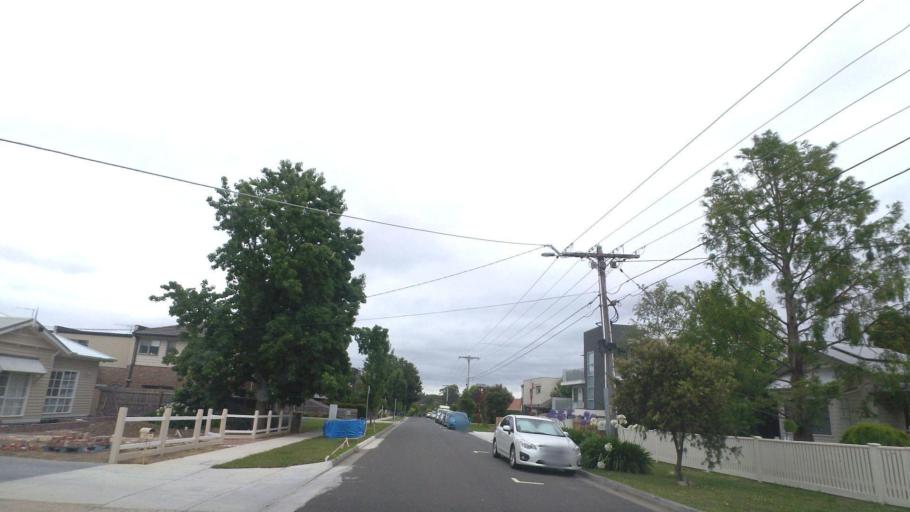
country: AU
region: Victoria
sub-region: Knox
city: Boronia
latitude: -37.8629
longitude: 145.2792
